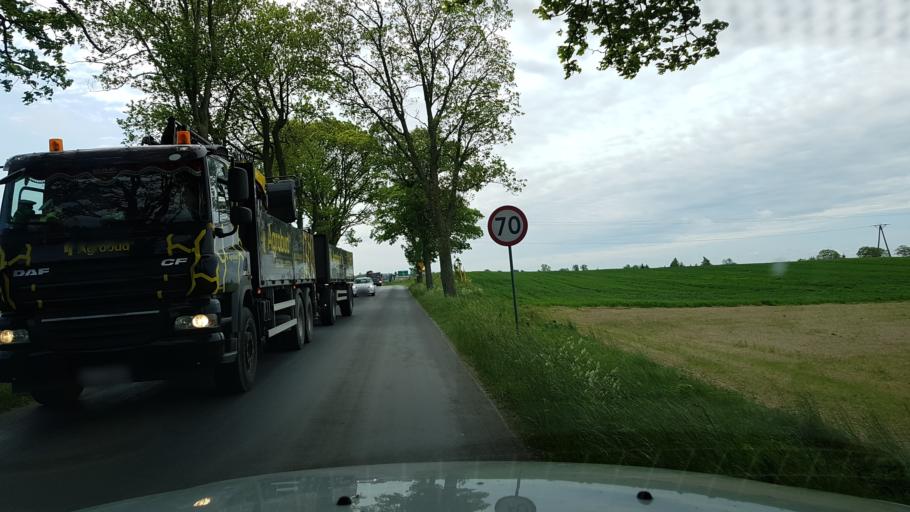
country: PL
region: West Pomeranian Voivodeship
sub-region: Powiat koszalinski
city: Mielno
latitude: 54.2406
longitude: 15.9733
